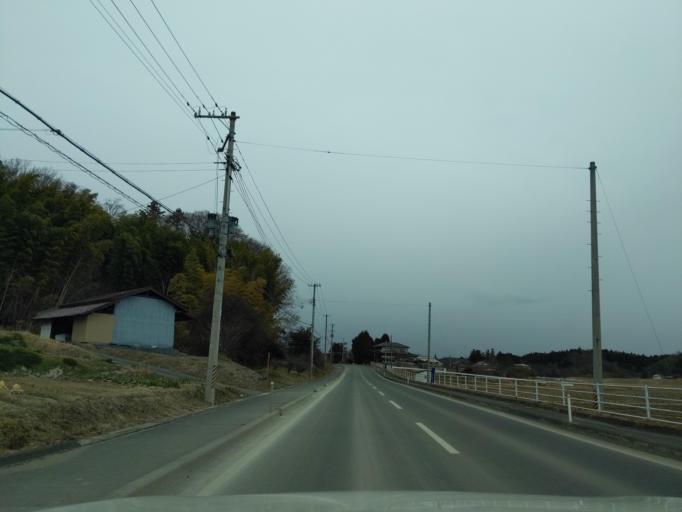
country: JP
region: Fukushima
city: Koriyama
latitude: 37.4380
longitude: 140.4165
